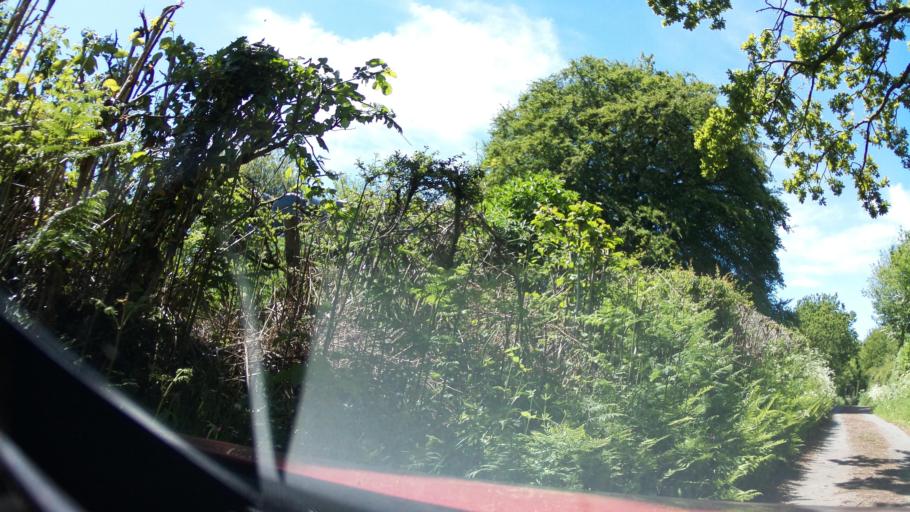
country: GB
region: Wales
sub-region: Monmouthshire
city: Llangwm
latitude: 51.6715
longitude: -2.7688
